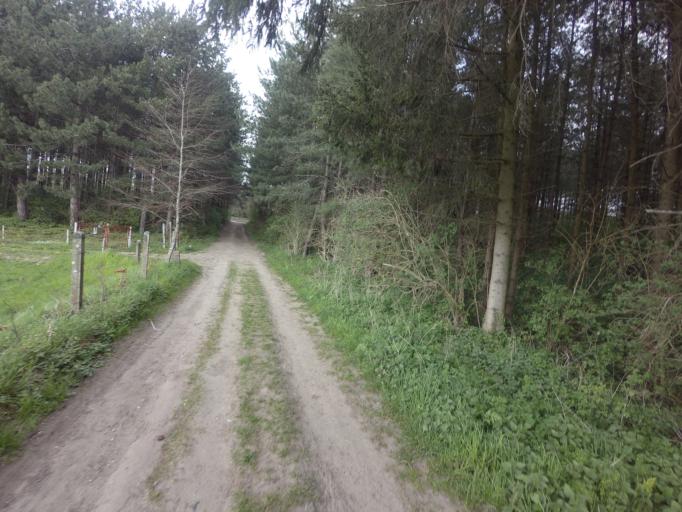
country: BE
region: Wallonia
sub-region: Province de Liege
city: La Calamine
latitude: 50.7301
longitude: 6.0070
